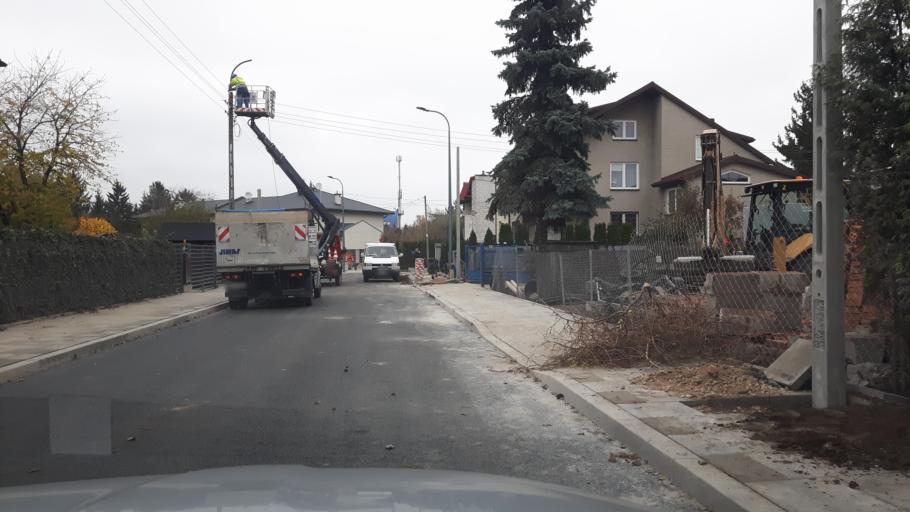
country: PL
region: Masovian Voivodeship
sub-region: Warszawa
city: Targowek
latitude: 52.2817
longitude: 21.0686
